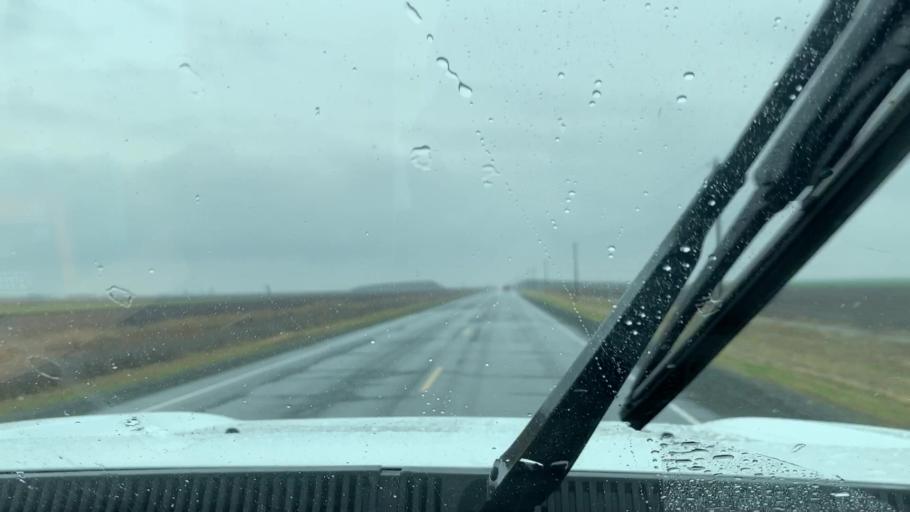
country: US
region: California
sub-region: Tulare County
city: Alpaugh
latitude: 35.9387
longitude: -119.4398
